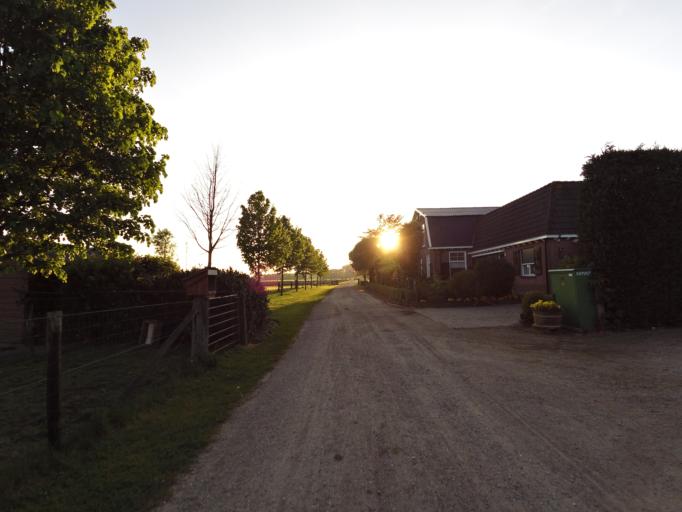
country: NL
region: Gelderland
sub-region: Oude IJsselstreek
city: Varsseveld
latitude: 51.9105
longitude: 6.4691
